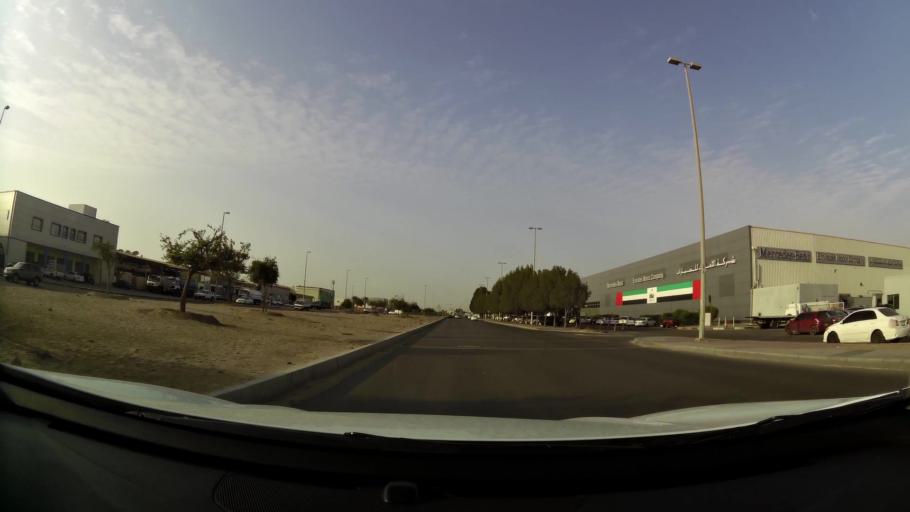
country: AE
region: Abu Dhabi
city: Abu Dhabi
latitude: 24.3667
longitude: 54.5164
